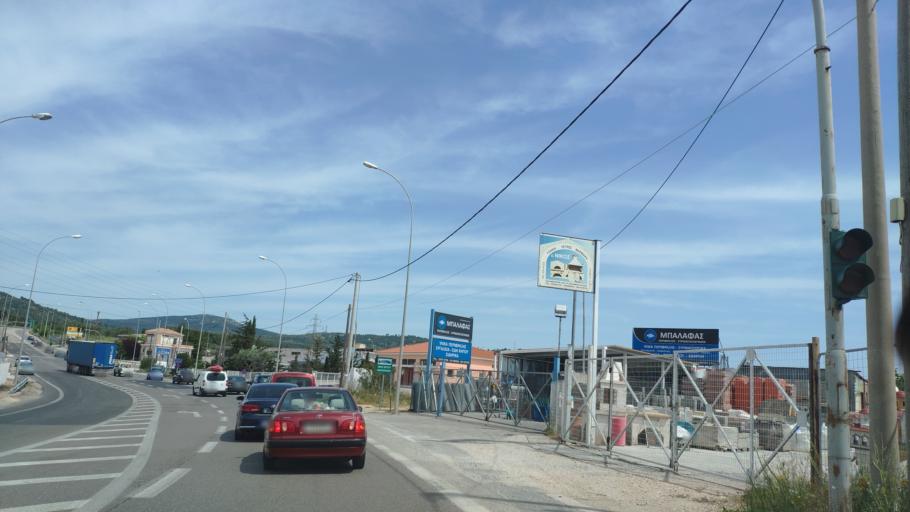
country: GR
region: Attica
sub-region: Nomarchia Anatolikis Attikis
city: Polydendri
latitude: 38.2013
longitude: 23.8576
